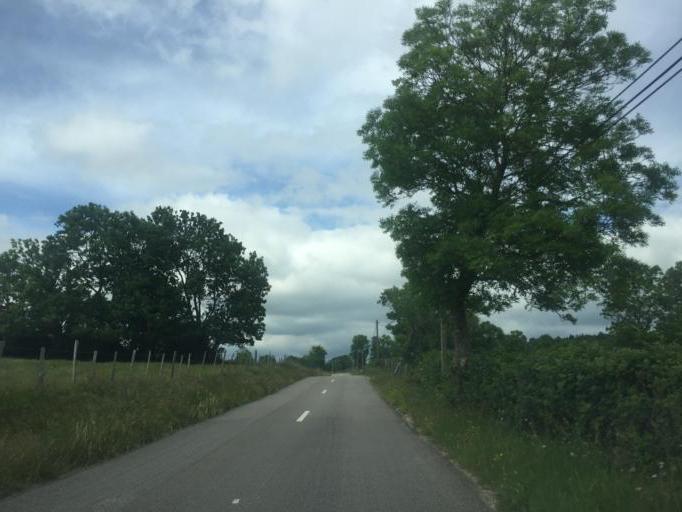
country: FR
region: Rhone-Alpes
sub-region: Departement de l'Ardeche
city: Saint-Priest
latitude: 44.6469
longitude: 4.5609
